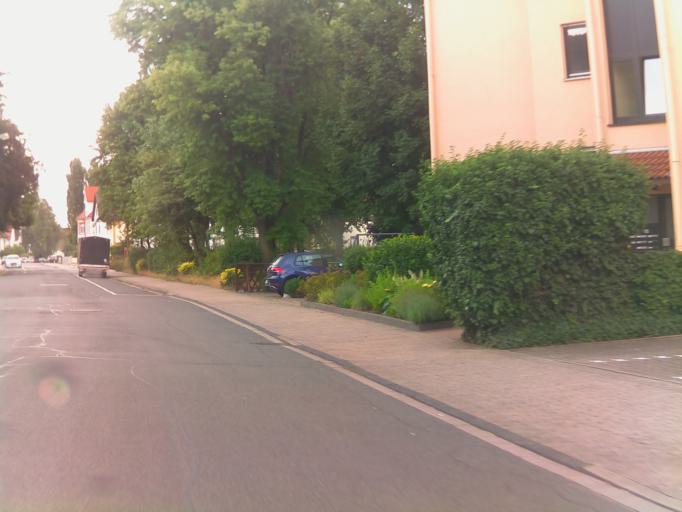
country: DE
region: Hesse
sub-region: Regierungsbezirk Darmstadt
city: Heppenheim an der Bergstrasse
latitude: 49.6472
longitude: 8.6363
